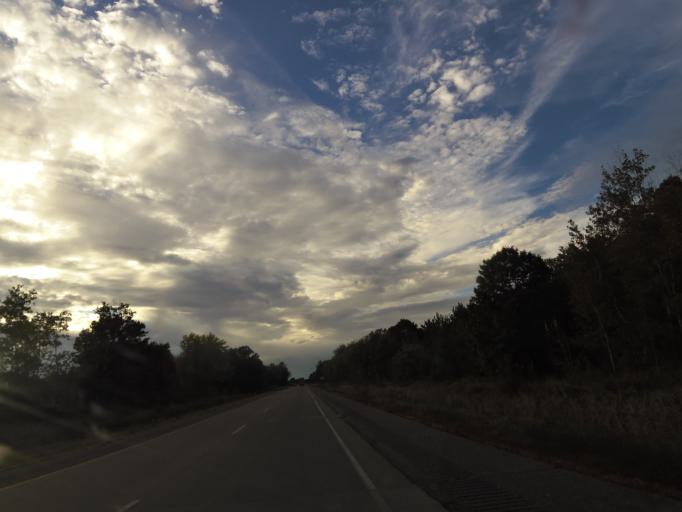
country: US
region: Wisconsin
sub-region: Juneau County
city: Mauston
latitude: 43.7707
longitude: -89.9999
